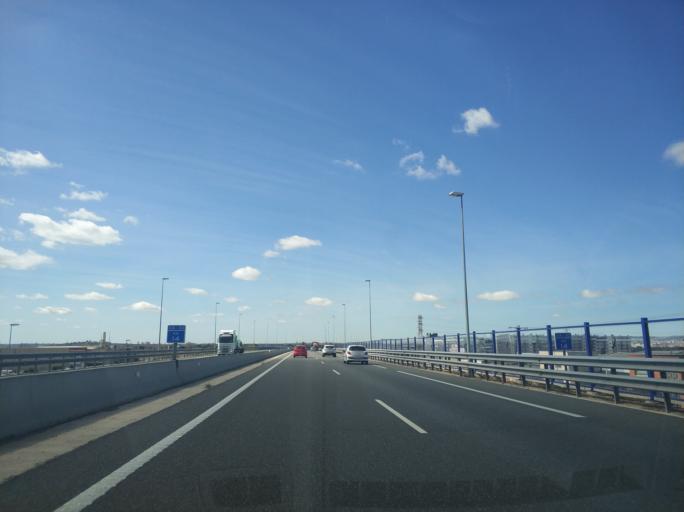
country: ES
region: Castille and Leon
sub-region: Provincia de Valladolid
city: Cisterniga
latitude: 41.6142
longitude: -4.7093
